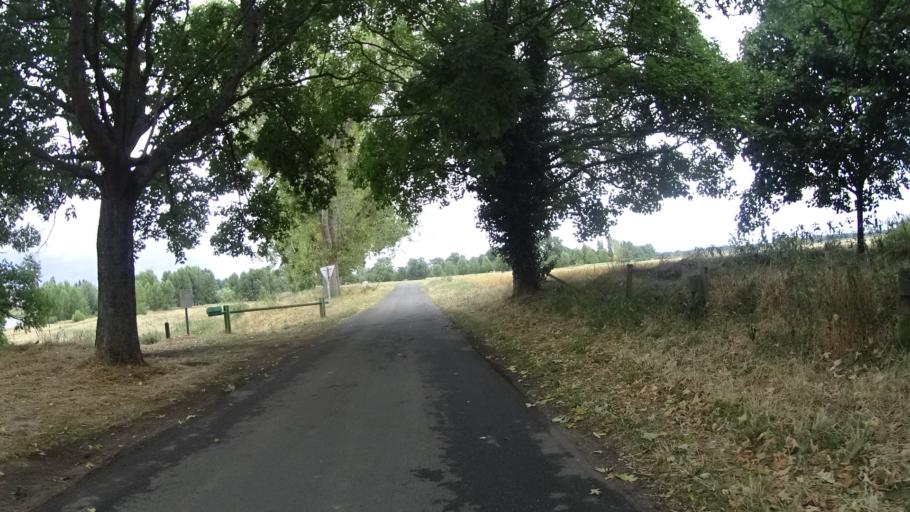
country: FR
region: Centre
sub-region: Departement du Loiret
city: Meung-sur-Loire
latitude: 47.8225
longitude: 1.7048
